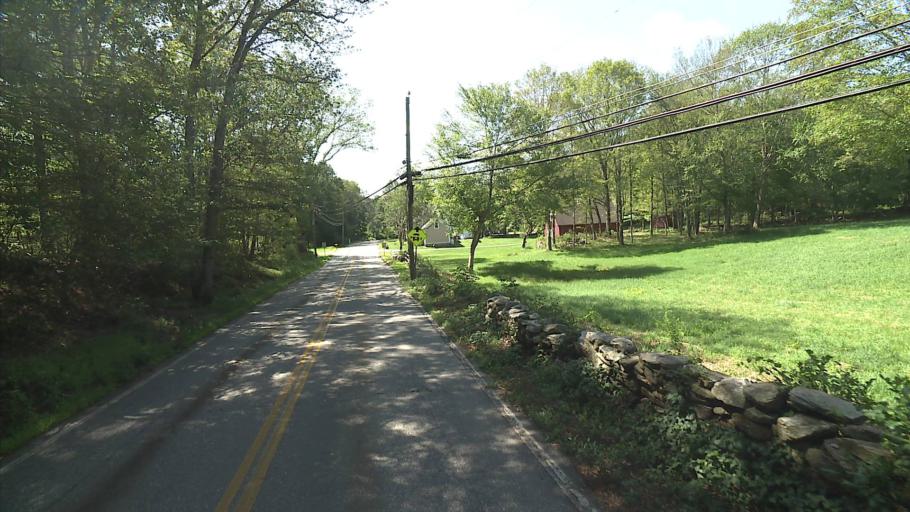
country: US
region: Connecticut
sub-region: Tolland County
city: Storrs
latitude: 41.8285
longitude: -72.1700
